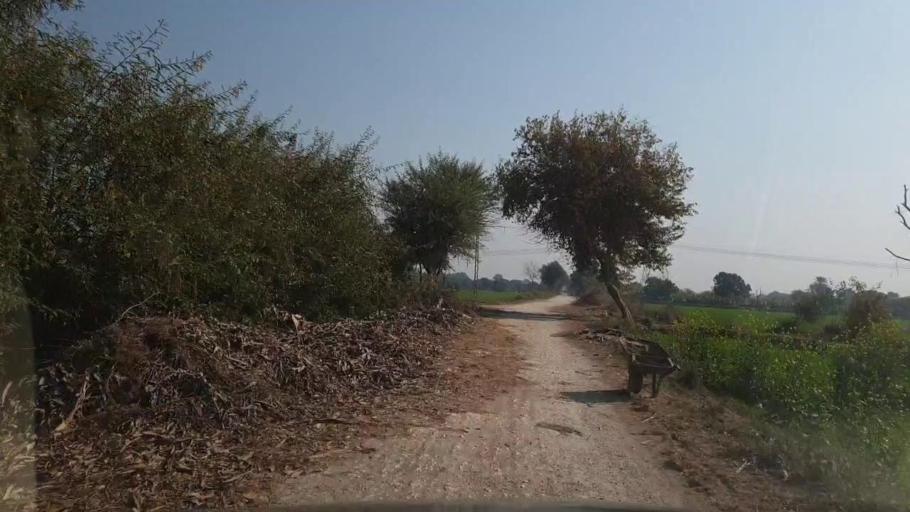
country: PK
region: Sindh
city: Matiari
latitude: 25.5445
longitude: 68.4895
